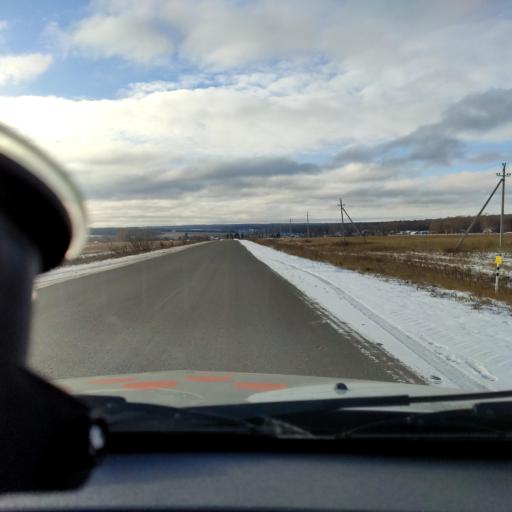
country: RU
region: Bashkortostan
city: Mikhaylovka
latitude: 54.8092
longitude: 55.7834
